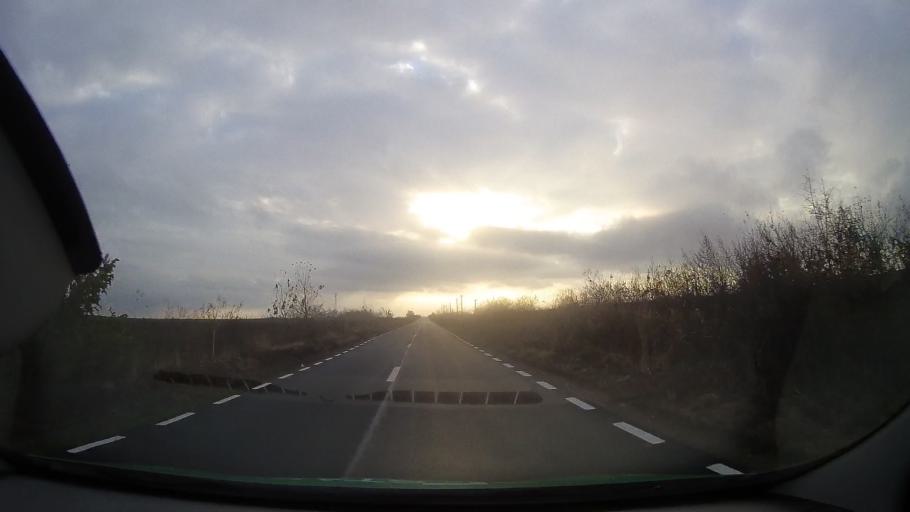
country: RO
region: Constanta
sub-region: Comuna Adamclisi
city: Adamclisi
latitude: 44.0730
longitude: 27.9858
